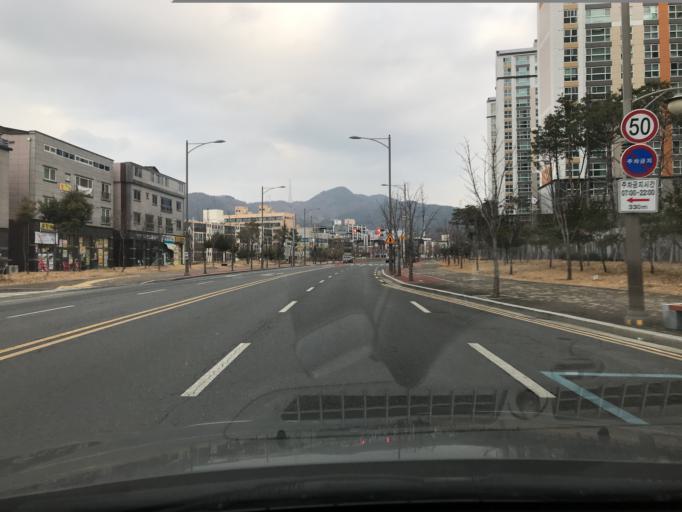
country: KR
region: Daegu
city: Hwawon
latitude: 35.6926
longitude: 128.4496
